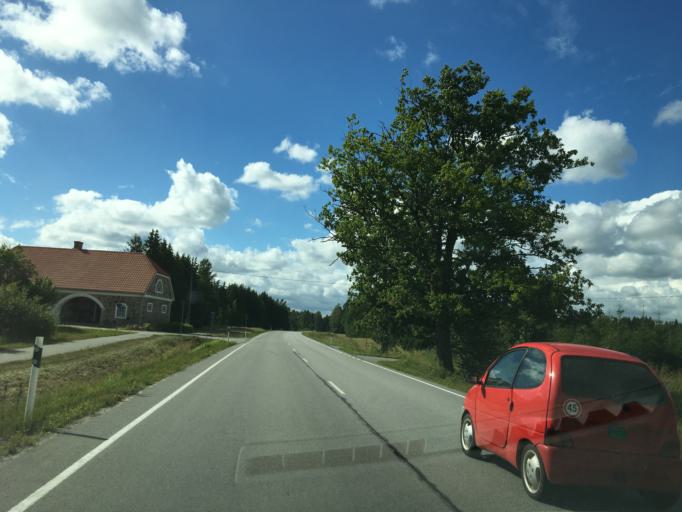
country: EE
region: Paernumaa
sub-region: Vaendra vald (alev)
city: Vandra
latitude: 58.6523
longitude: 25.0634
